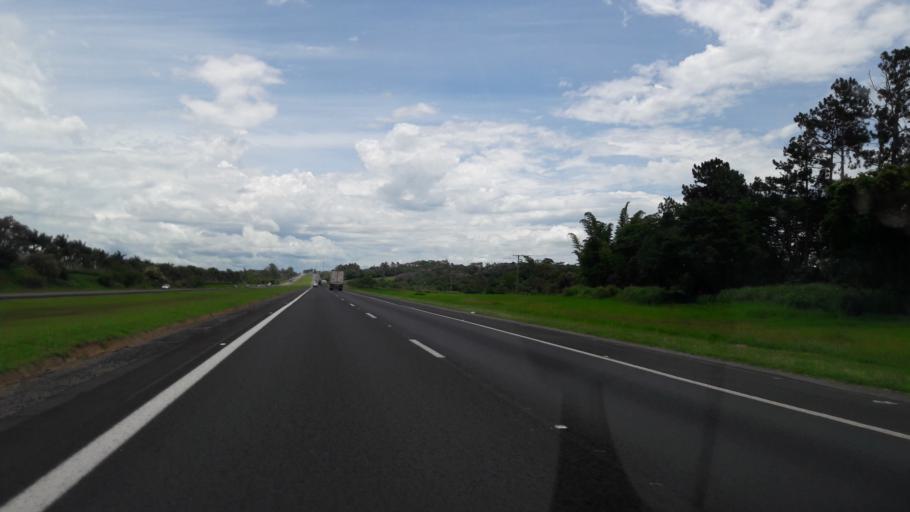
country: BR
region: Sao Paulo
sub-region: Porangaba
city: Porangaba
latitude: -23.2479
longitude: -48.0172
